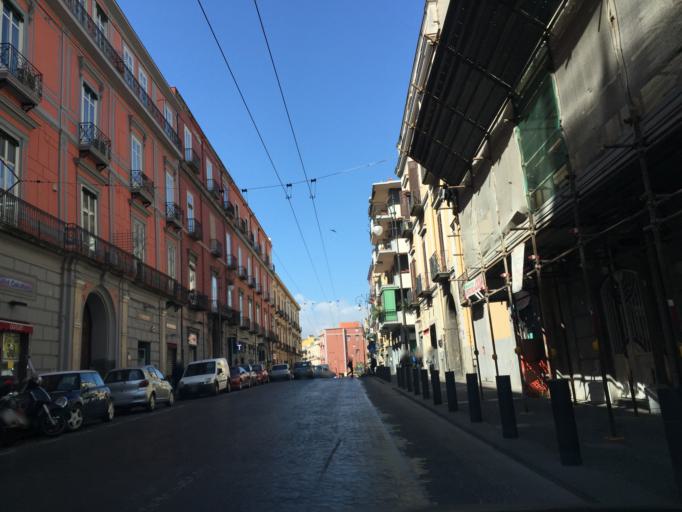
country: IT
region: Campania
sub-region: Provincia di Napoli
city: Portici
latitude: 40.8153
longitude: 14.3351
